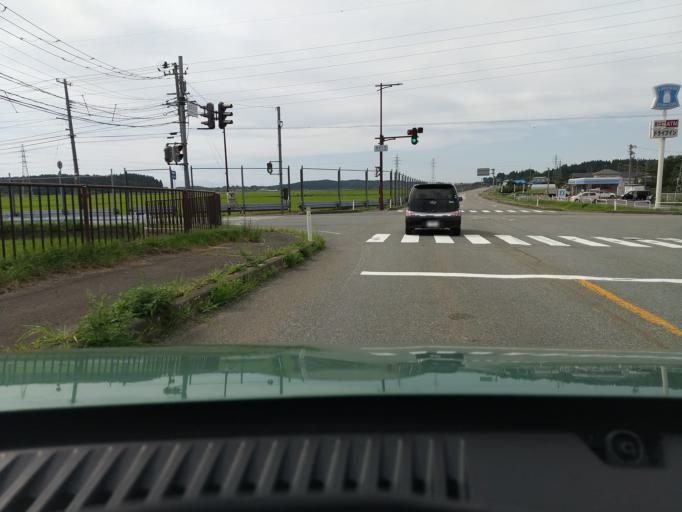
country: JP
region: Akita
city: Akita Shi
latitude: 39.8155
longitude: 140.0869
